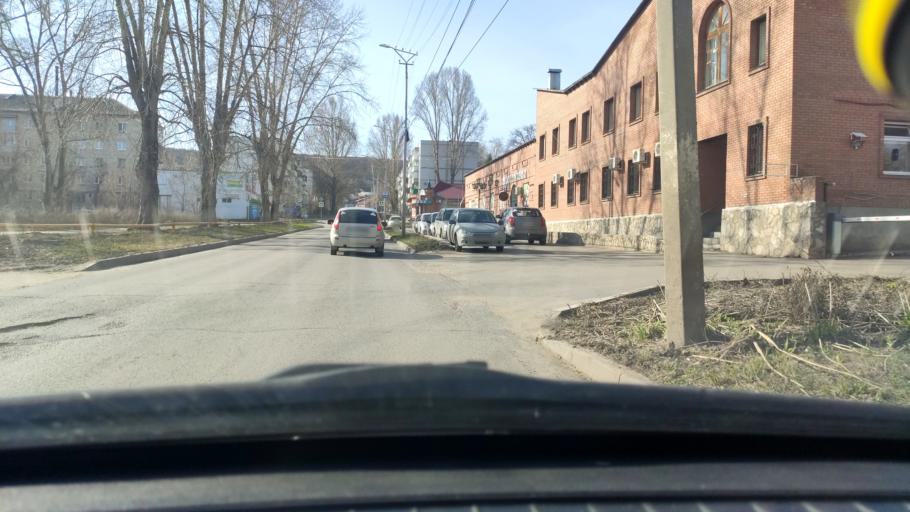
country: RU
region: Samara
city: Zhigulevsk
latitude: 53.3972
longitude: 49.4975
